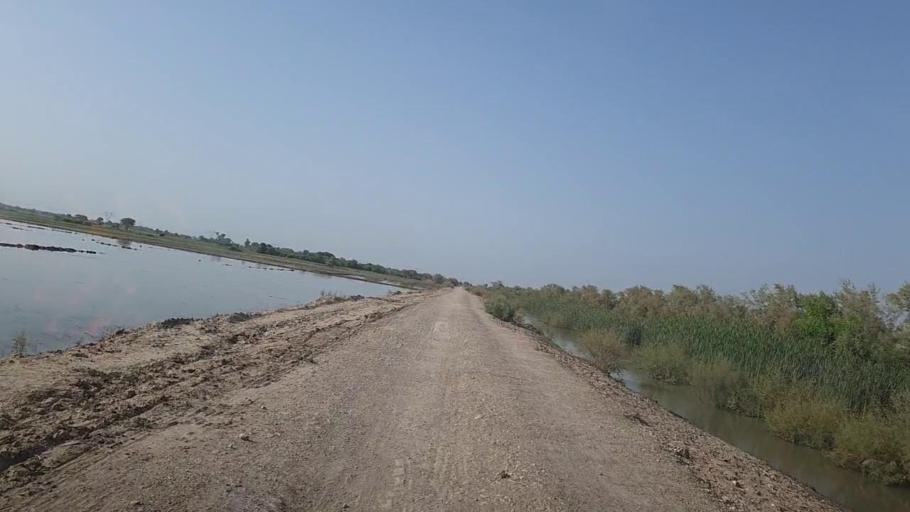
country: PK
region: Sindh
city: Sita Road
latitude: 27.0973
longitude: 67.8731
